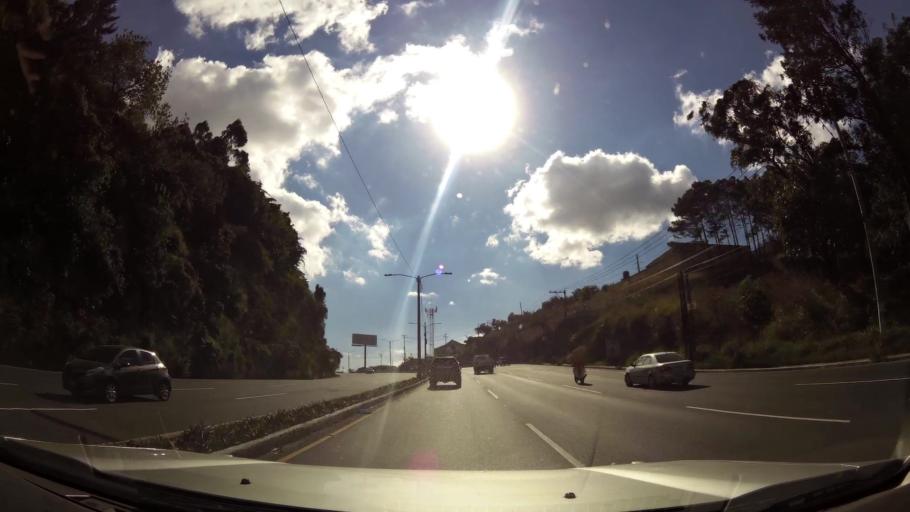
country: GT
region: Guatemala
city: Villa Nueva
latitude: 14.5437
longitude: -90.5831
